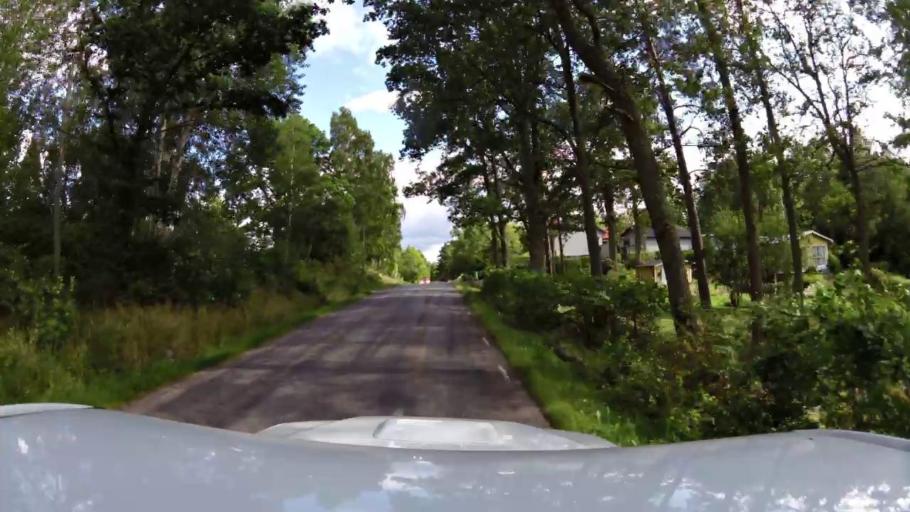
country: SE
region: OEstergoetland
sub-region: Kinda Kommun
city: Rimforsa
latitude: 58.2300
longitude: 15.6945
